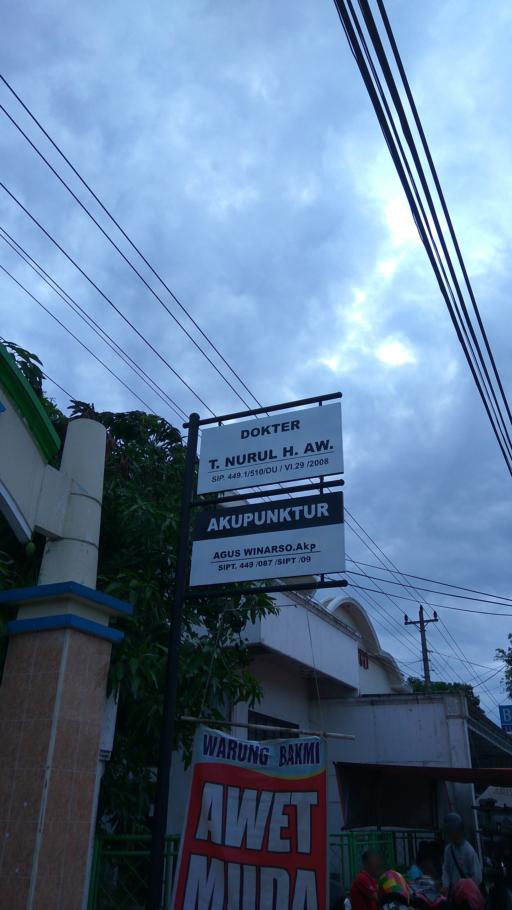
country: ID
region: Central Java
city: Baki
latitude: -7.5681
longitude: 110.7866
